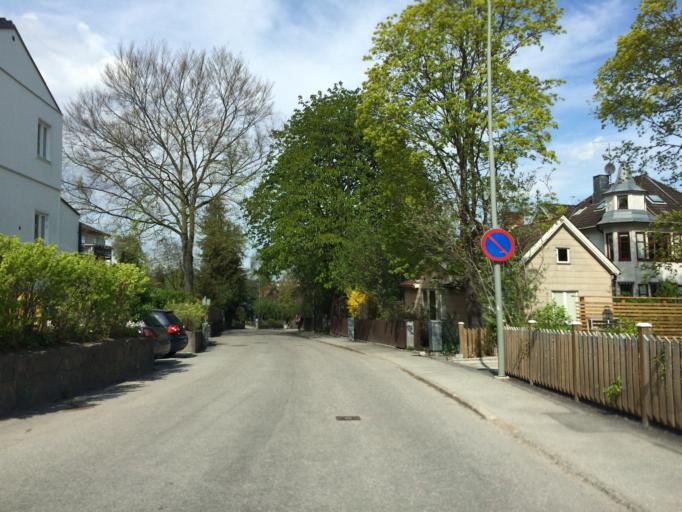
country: SE
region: Stockholm
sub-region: Huddinge Kommun
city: Segeltorp
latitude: 59.3021
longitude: 17.9561
